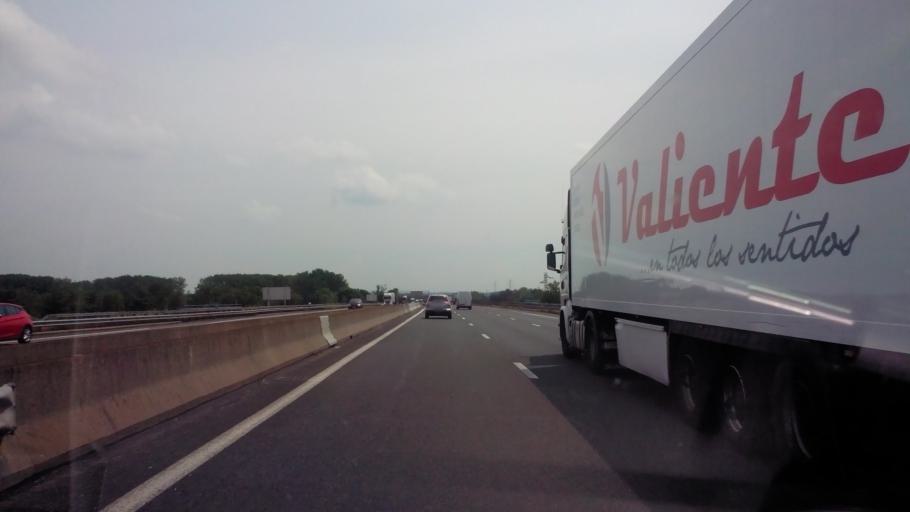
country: FR
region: Bourgogne
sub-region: Departement de Saone-et-Loire
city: Creches-sur-Saone
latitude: 46.2636
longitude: 4.7913
